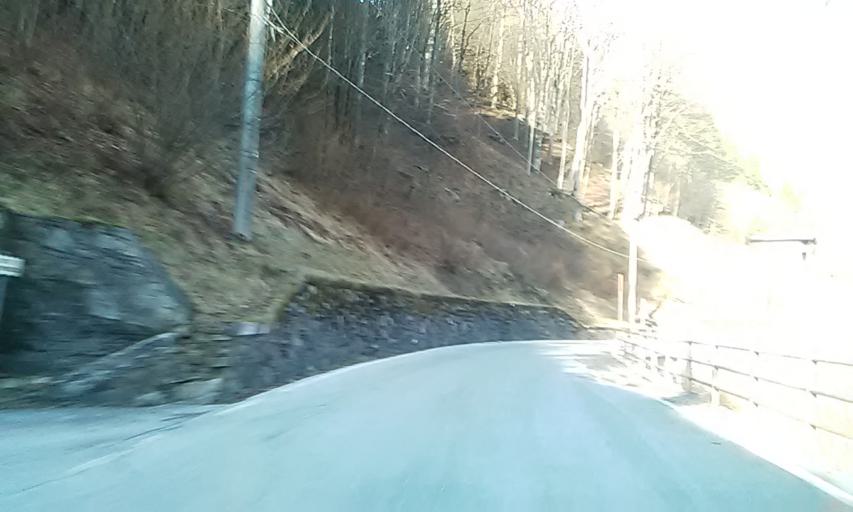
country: IT
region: Piedmont
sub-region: Provincia di Vercelli
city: Rimasco
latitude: 45.8554
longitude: 8.0635
